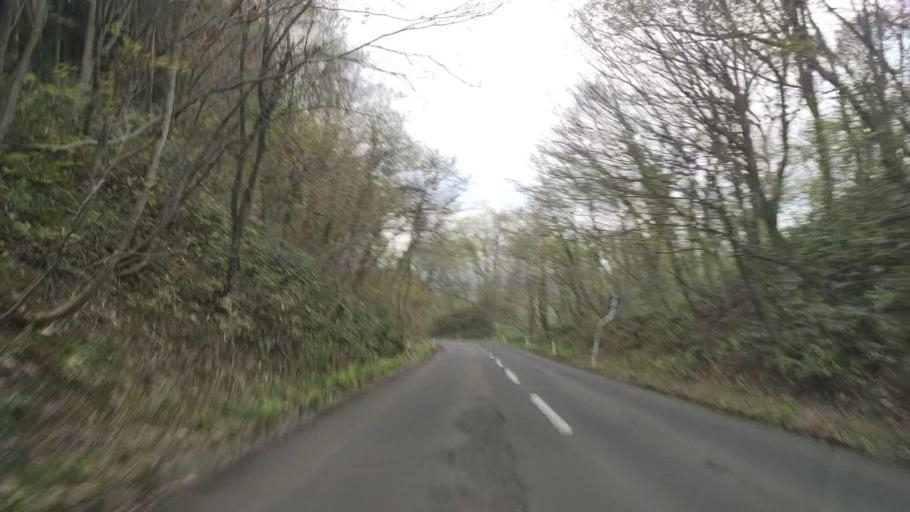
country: JP
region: Akita
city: Hanawa
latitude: 40.3828
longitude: 140.7914
